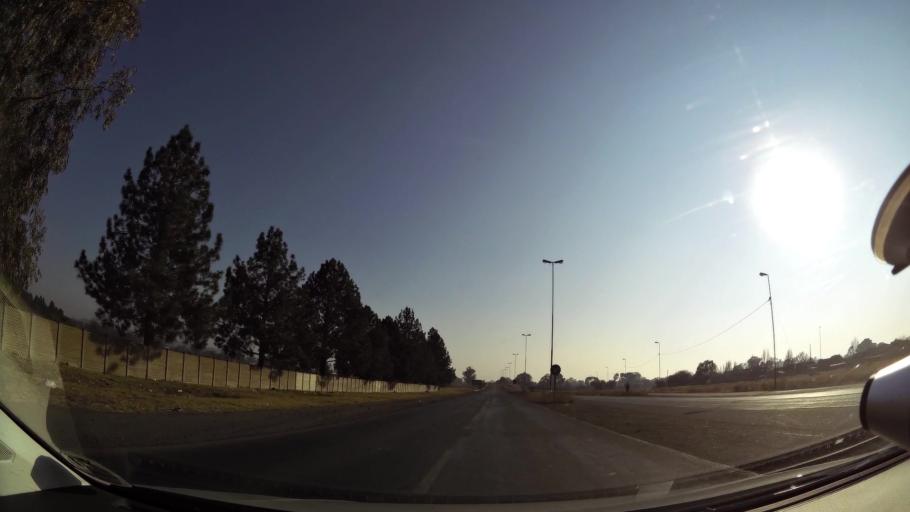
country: ZA
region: Orange Free State
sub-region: Mangaung Metropolitan Municipality
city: Bloemfontein
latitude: -29.1399
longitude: 26.2667
